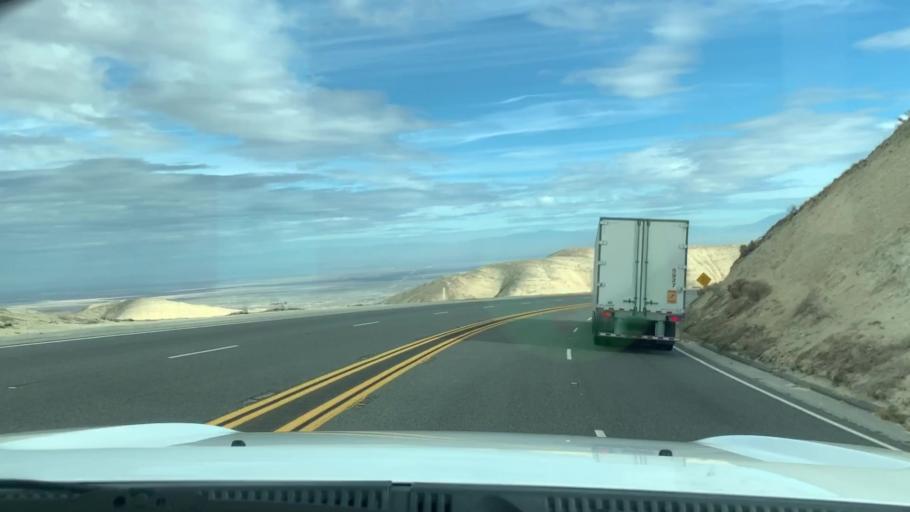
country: US
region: California
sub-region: Kern County
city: Maricopa
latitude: 35.0046
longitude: -119.4200
